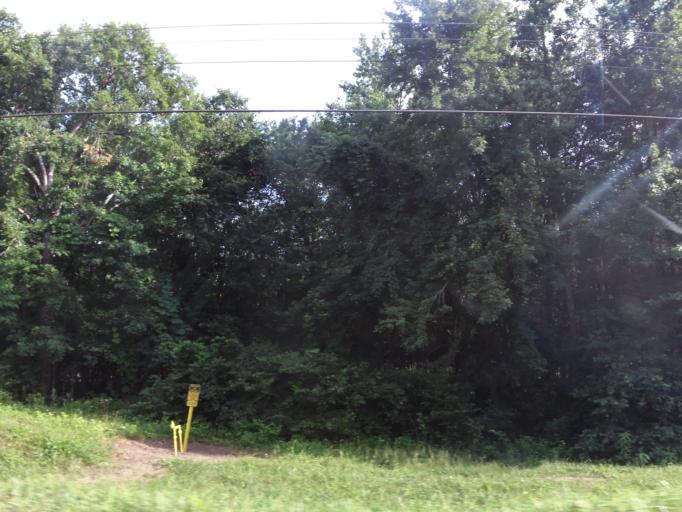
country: US
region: Tennessee
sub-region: Benton County
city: Camden
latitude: 36.0454
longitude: -88.1566
